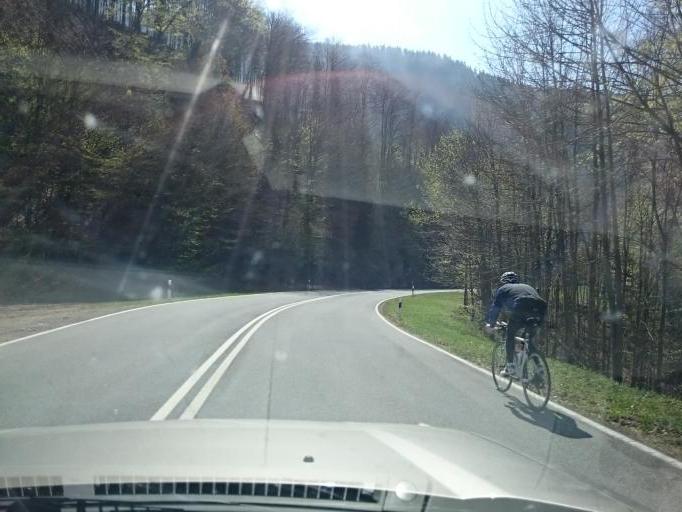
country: DE
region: Bavaria
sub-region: Upper Bavaria
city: Kochel
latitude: 47.6302
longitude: 11.3541
